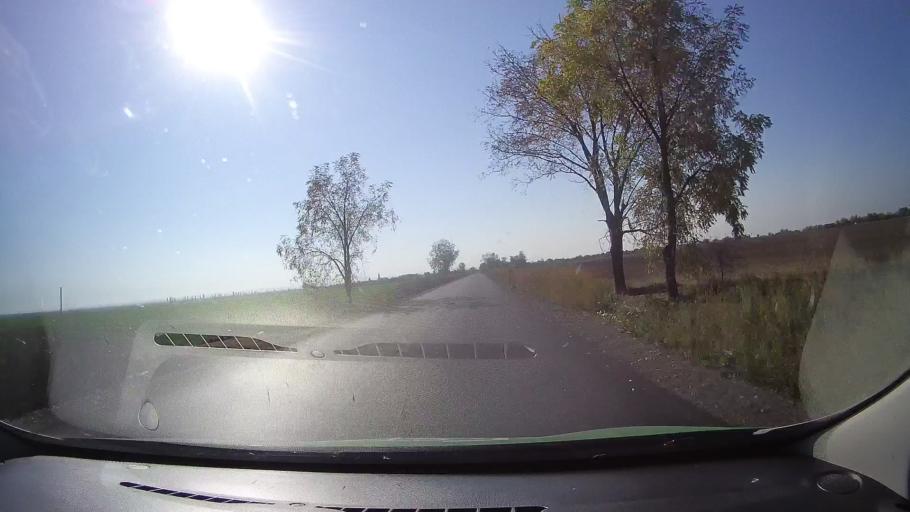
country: RO
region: Satu Mare
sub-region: Comuna Tiream
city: Tiream
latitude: 47.6268
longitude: 22.4677
